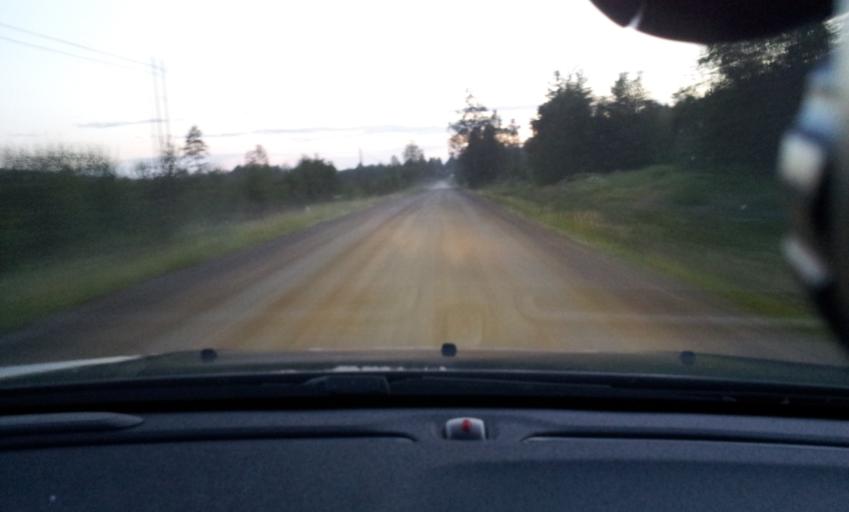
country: SE
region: Jaemtland
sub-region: Braecke Kommun
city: Braecke
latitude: 62.7221
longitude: 15.5475
